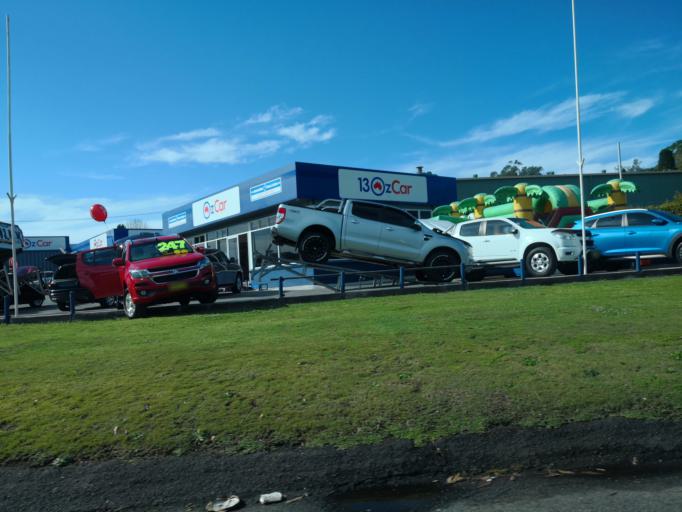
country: AU
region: New South Wales
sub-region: Gosford Shire
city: Narara
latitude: -33.4114
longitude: 151.3462
